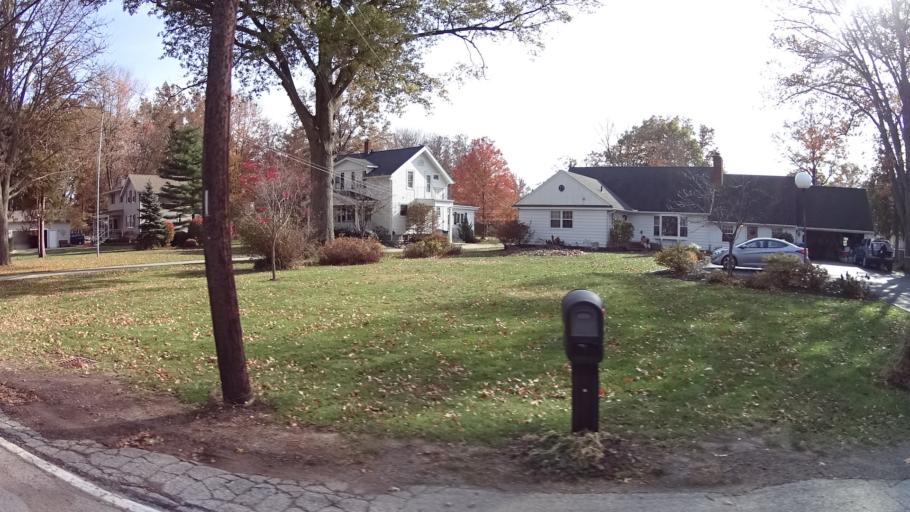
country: US
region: Ohio
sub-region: Lorain County
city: Avon Lake
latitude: 41.5090
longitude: -82.0336
